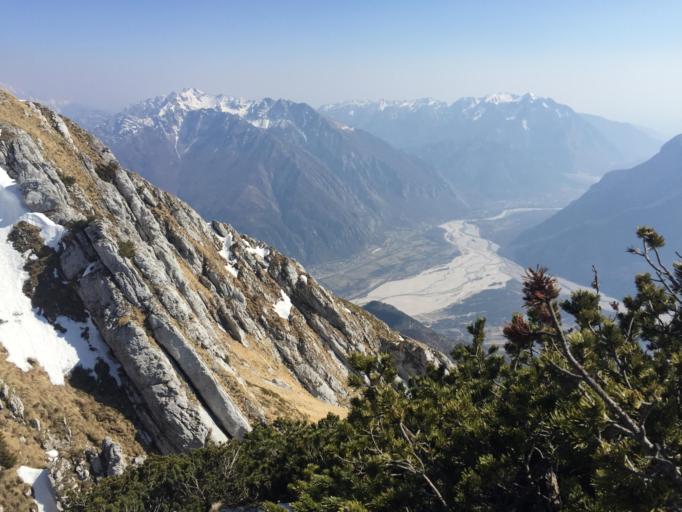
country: IT
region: Friuli Venezia Giulia
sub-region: Provincia di Udine
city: Amaro
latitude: 46.4004
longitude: 13.0821
